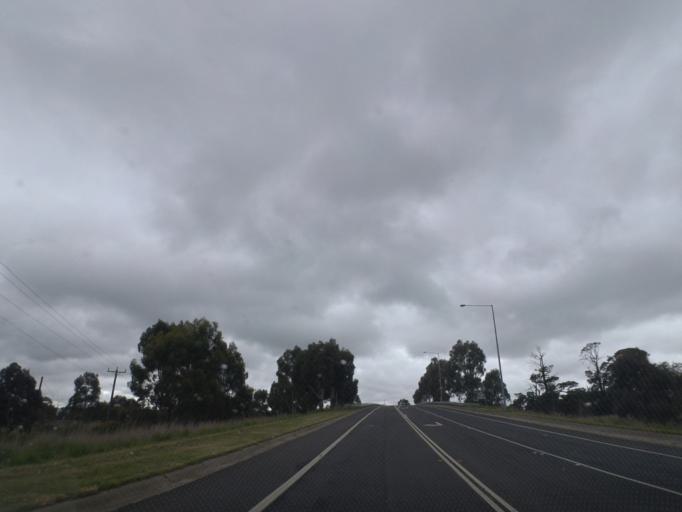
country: AU
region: Victoria
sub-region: Hume
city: Sunbury
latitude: -37.3222
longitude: 144.5246
